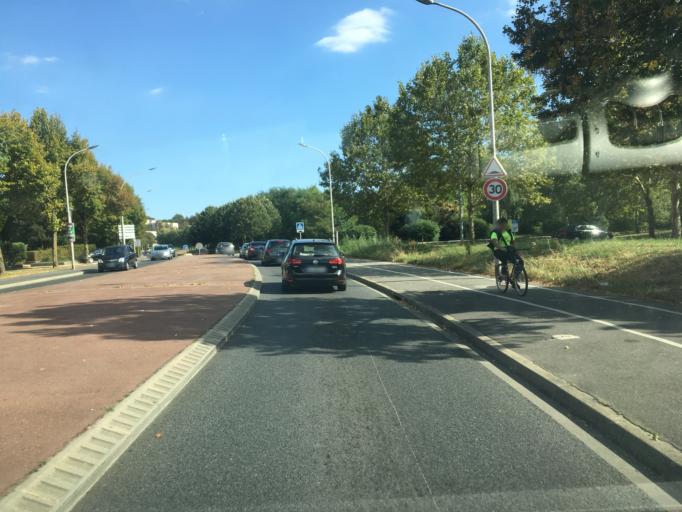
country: FR
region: Ile-de-France
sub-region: Departement du Val-de-Marne
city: Valenton
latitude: 48.7487
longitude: 2.4559
